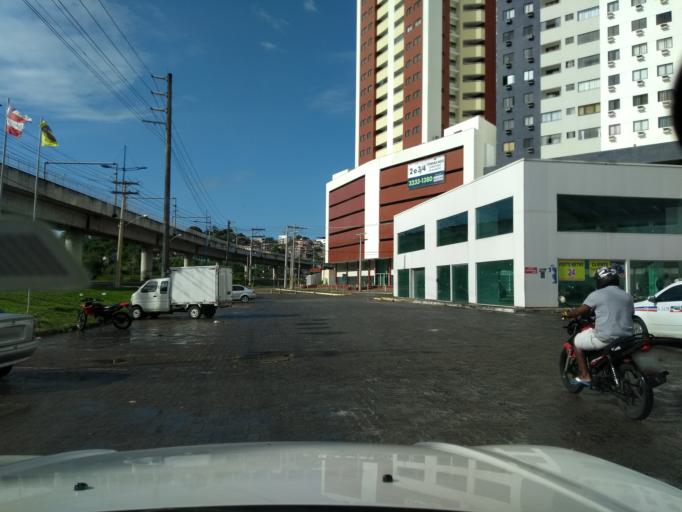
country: BR
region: Bahia
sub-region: Salvador
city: Salvador
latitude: -12.9732
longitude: -38.4781
